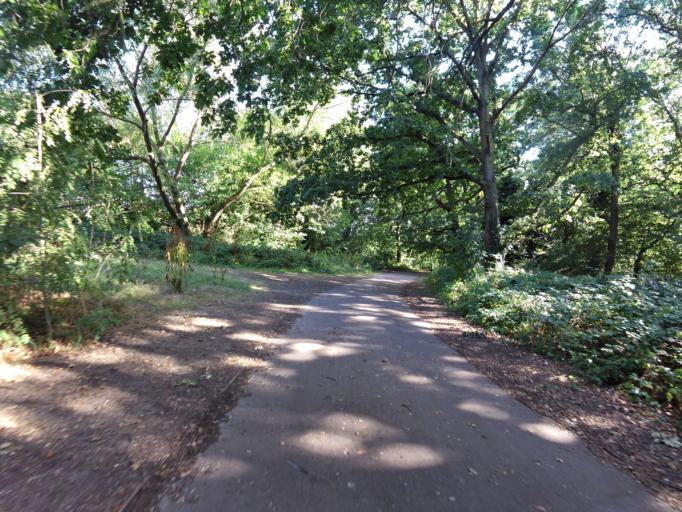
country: GB
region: England
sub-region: Greater London
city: Wood Green
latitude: 51.6274
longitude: -0.1421
